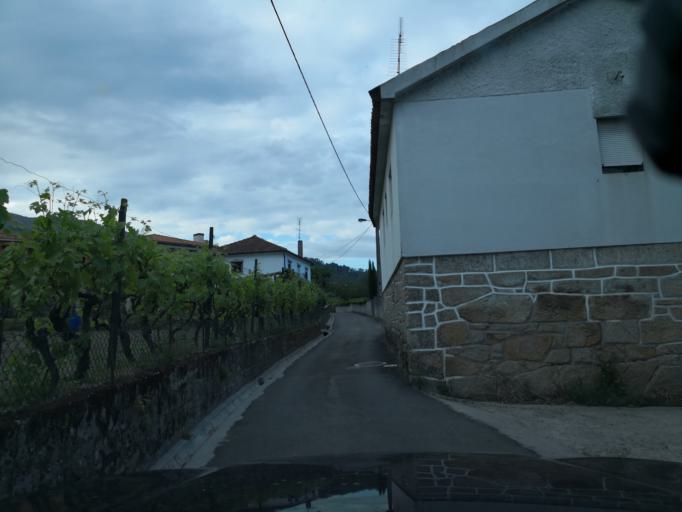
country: PT
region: Vila Real
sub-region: Vila Real
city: Vila Real
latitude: 41.3235
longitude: -7.7468
